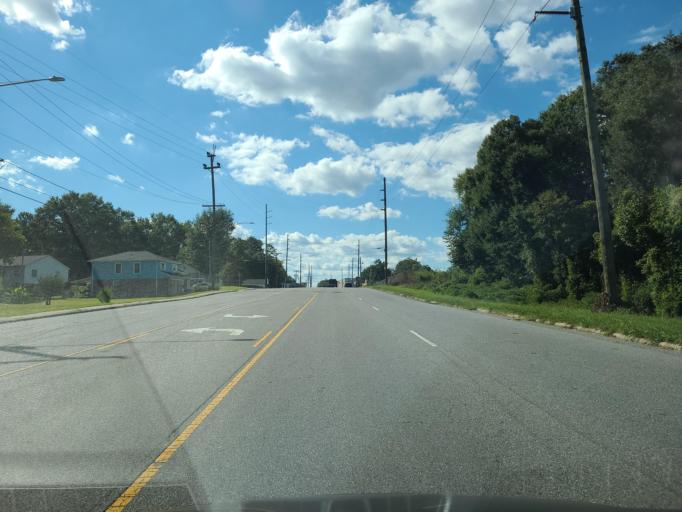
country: US
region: North Carolina
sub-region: Gaston County
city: Gastonia
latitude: 35.2571
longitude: -81.2031
